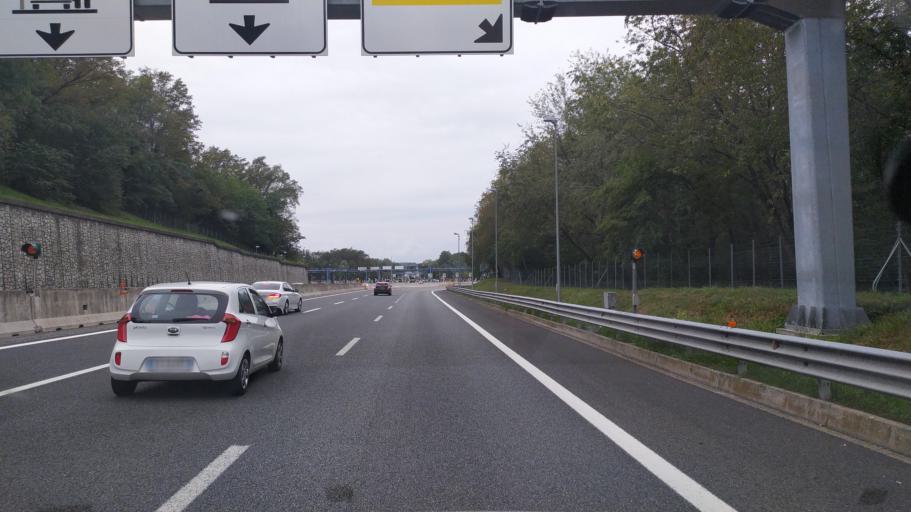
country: IT
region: Lombardy
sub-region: Provincia di Varese
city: Besnate
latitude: 45.6877
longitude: 8.7804
